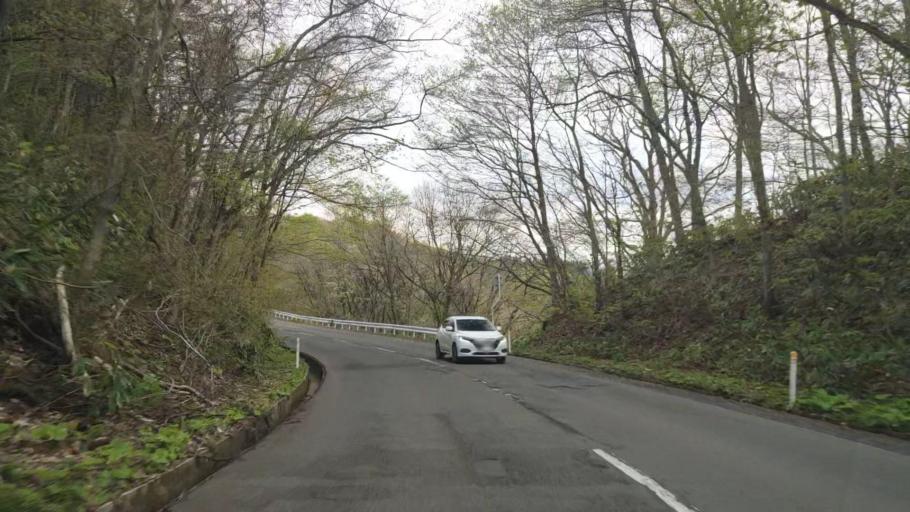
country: JP
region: Akita
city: Hanawa
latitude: 40.3819
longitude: 140.7908
